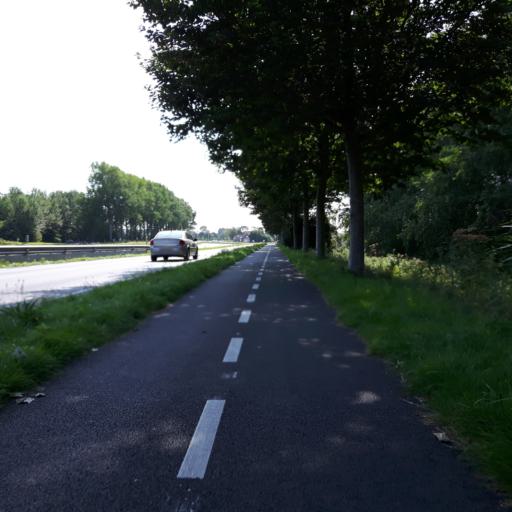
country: NL
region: Zeeland
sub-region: Gemeente Goes
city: Goes
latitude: 51.5233
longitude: 3.8942
